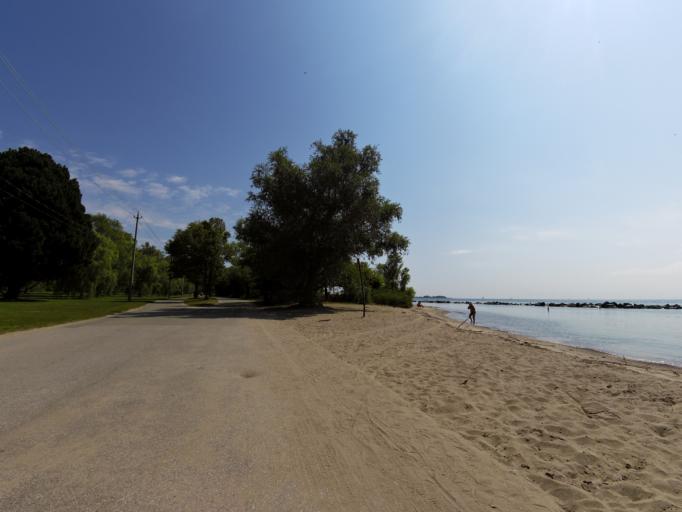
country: CA
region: Ontario
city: Toronto
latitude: 43.6146
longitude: -79.3770
